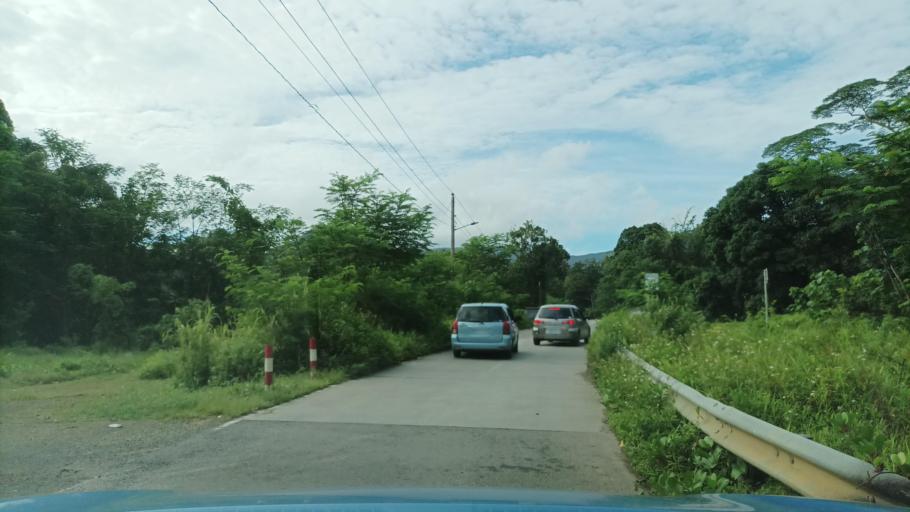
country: FM
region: Pohnpei
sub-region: Kolonia Municipality
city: Kolonia
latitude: 6.9460
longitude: 158.2246
